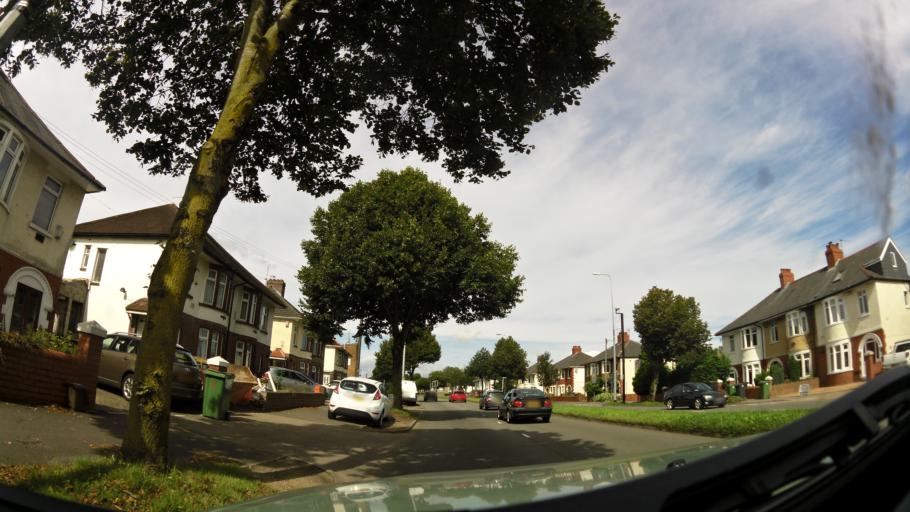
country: GB
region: Wales
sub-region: Cardiff
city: Cardiff
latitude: 51.5110
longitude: -3.2049
